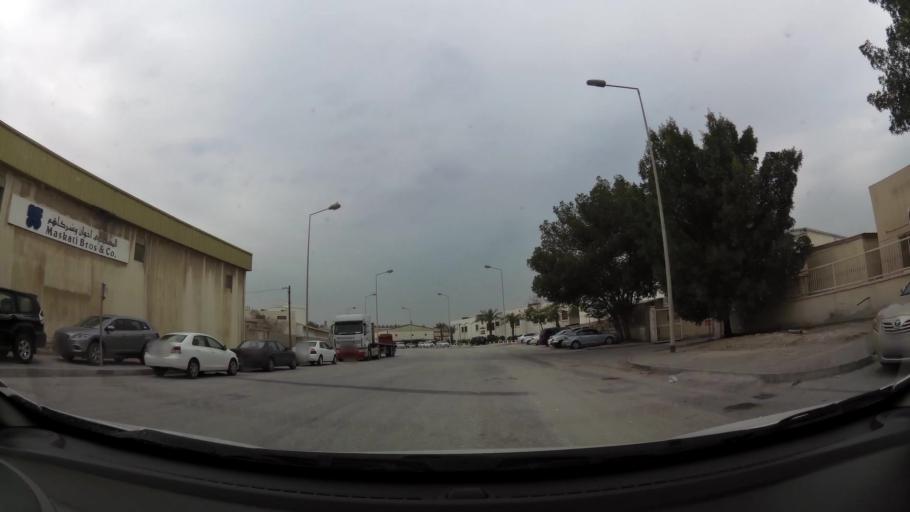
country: BH
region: Northern
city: Sitrah
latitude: 26.1830
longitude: 50.6182
